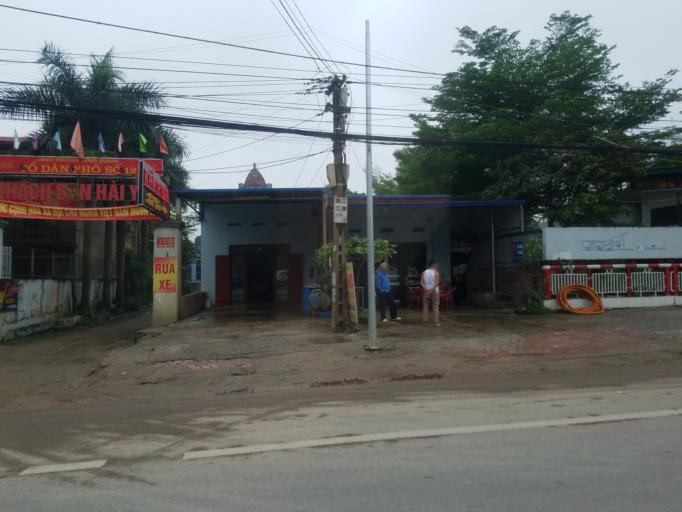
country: VN
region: Thai Nguyen
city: Thanh Pho Thai Nguyen
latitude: 21.5804
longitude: 105.8376
